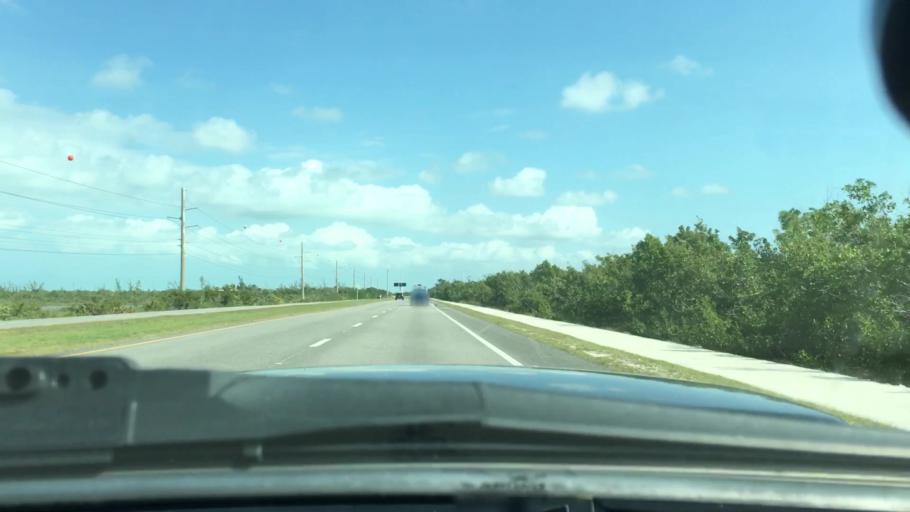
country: US
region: Florida
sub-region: Monroe County
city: Stock Island
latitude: 24.5829
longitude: -81.7020
